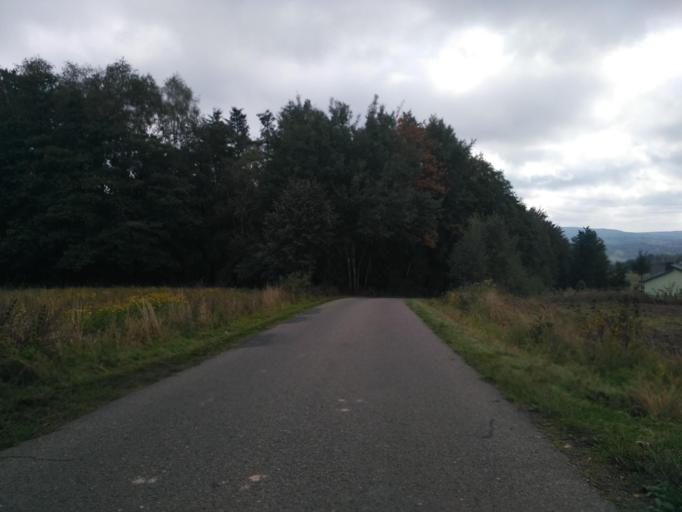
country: PL
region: Subcarpathian Voivodeship
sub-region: Powiat ropczycko-sedziszowski
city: Niedzwiada
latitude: 49.9534
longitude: 21.4578
